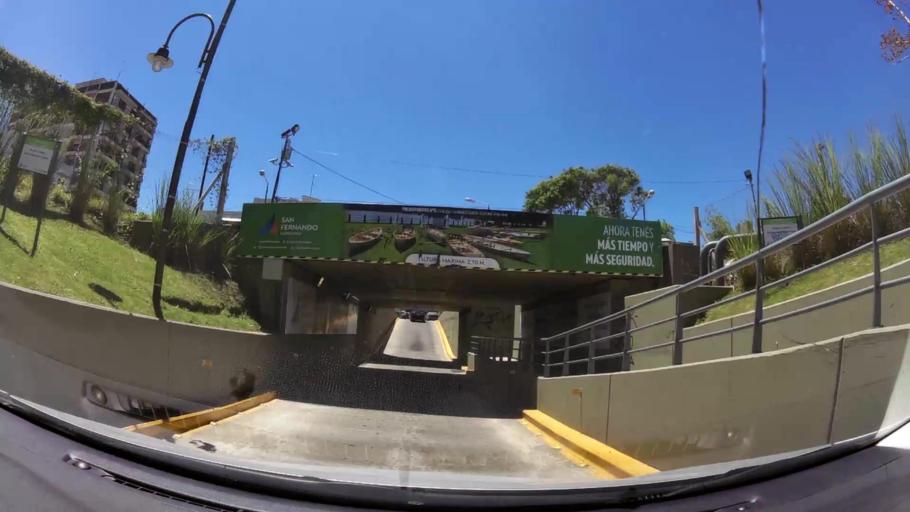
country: AR
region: Buenos Aires
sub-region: Partido de Tigre
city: Tigre
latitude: -34.4457
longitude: -58.5573
